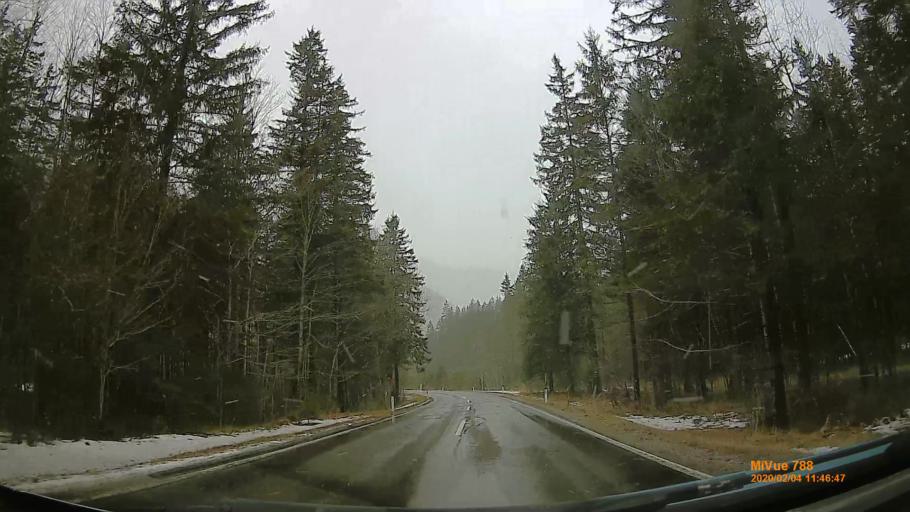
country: AT
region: Styria
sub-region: Politischer Bezirk Bruck-Muerzzuschlag
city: Muerzsteg
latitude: 47.7042
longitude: 15.4780
